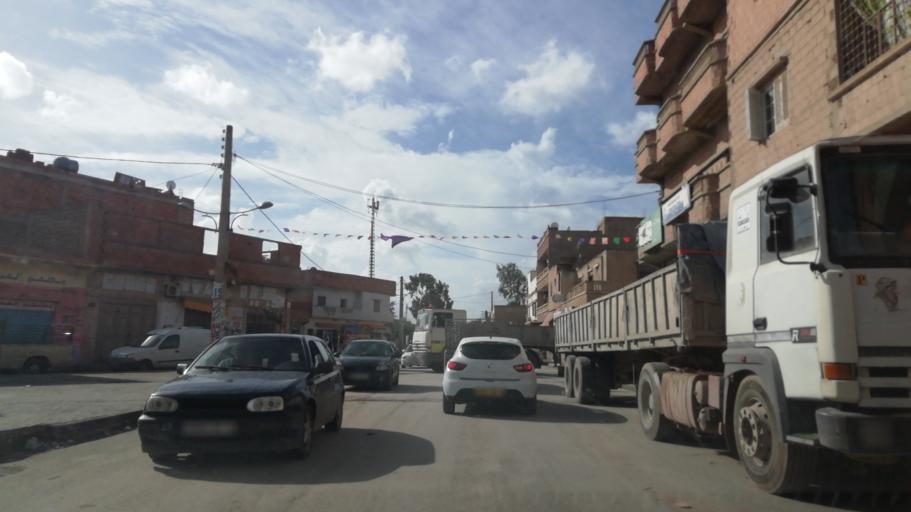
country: DZ
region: Oran
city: Sidi ech Chahmi
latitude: 35.6485
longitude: -0.5700
